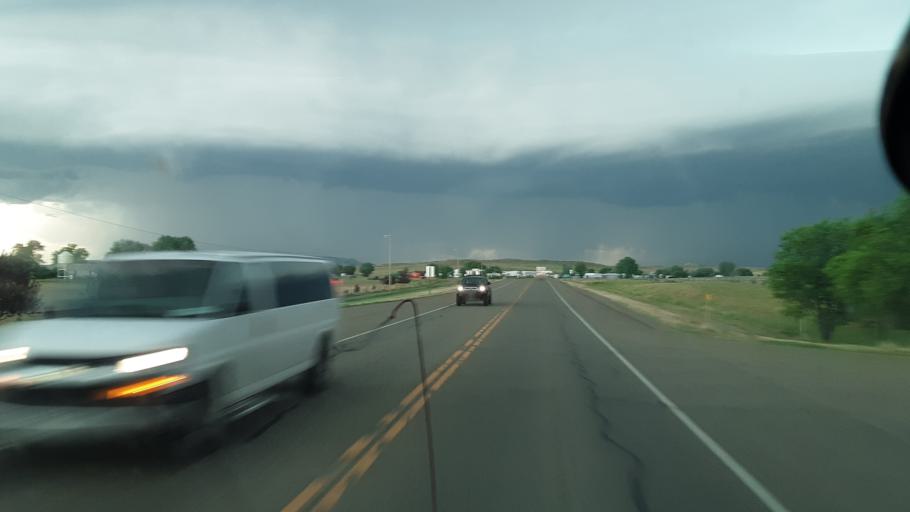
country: US
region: Montana
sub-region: Powder River County
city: Broadus
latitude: 45.4434
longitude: -105.4136
